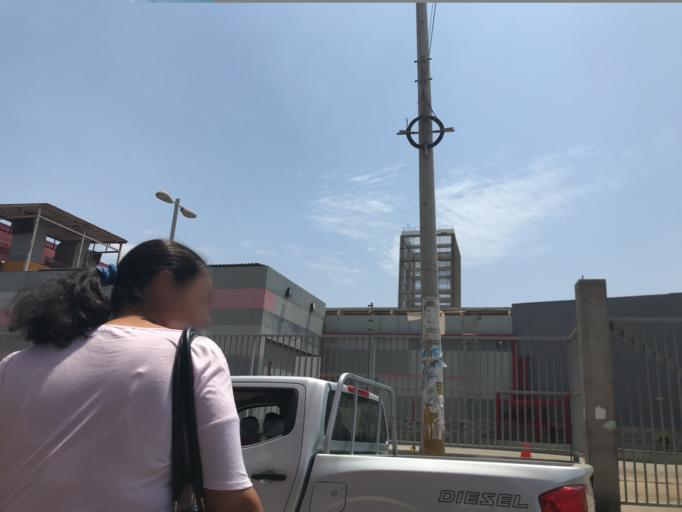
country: PE
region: Lambayeque
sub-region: Provincia de Chiclayo
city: Chiclayo
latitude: -6.7777
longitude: -79.8336
